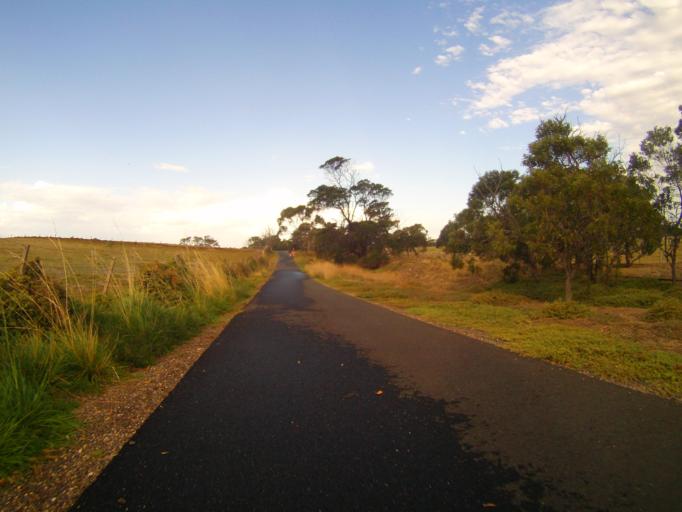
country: AU
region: Victoria
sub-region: Greater Geelong
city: Clifton Springs
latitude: -38.1787
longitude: 144.5450
